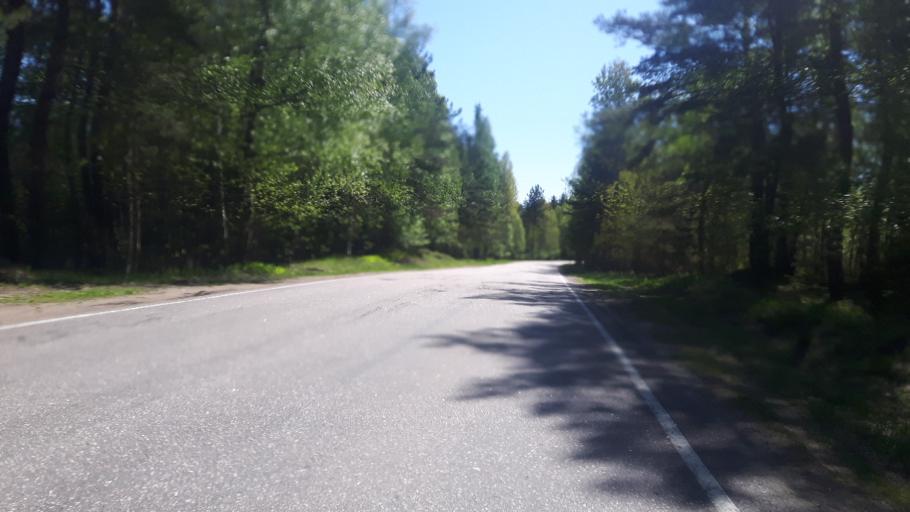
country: RU
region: Leningrad
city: Glebychevo
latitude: 60.3425
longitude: 28.8227
